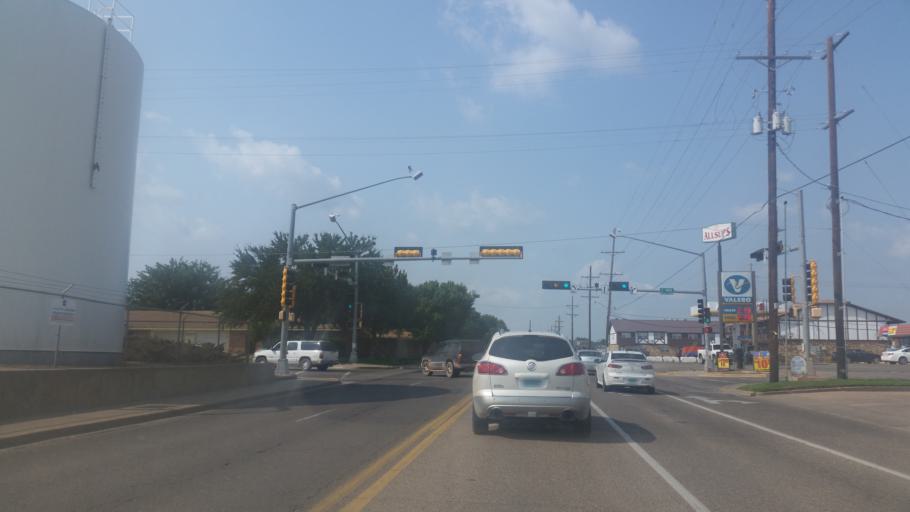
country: US
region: New Mexico
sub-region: Curry County
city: Clovis
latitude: 34.4117
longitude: -103.1789
